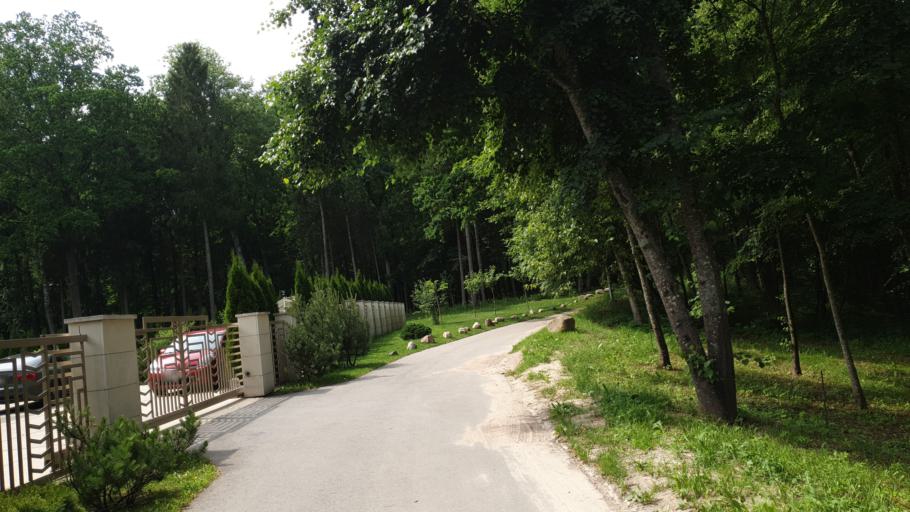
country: LT
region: Vilnius County
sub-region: Vilnius
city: Fabijoniskes
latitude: 54.7852
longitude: 25.3240
